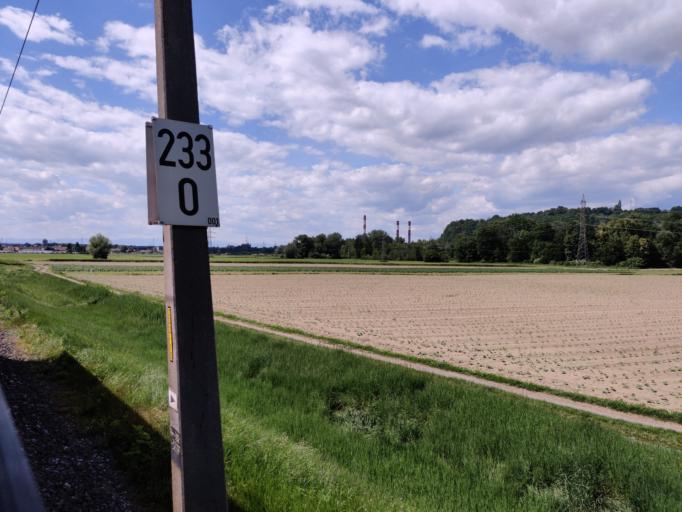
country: AT
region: Styria
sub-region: Politischer Bezirk Leibnitz
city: Wildon
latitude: 46.8926
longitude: 15.4990
